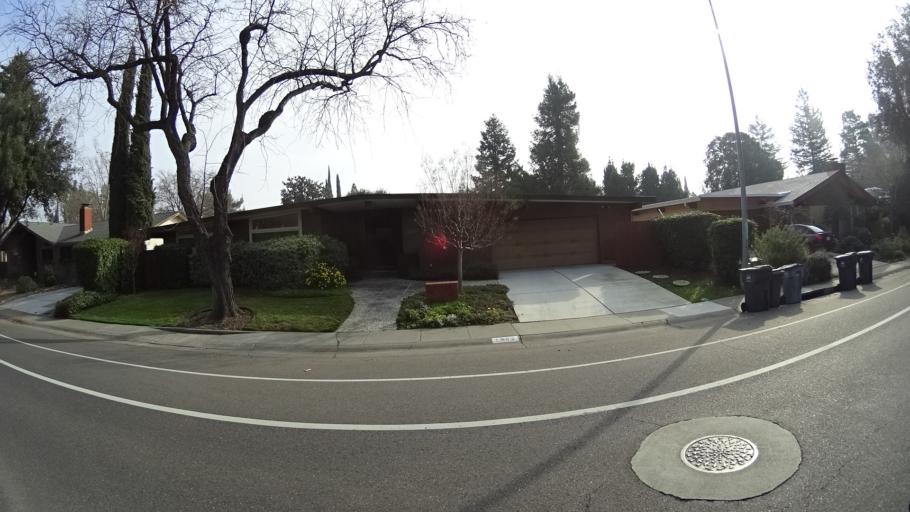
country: US
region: California
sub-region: Yolo County
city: Davis
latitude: 38.5579
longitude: -121.7650
